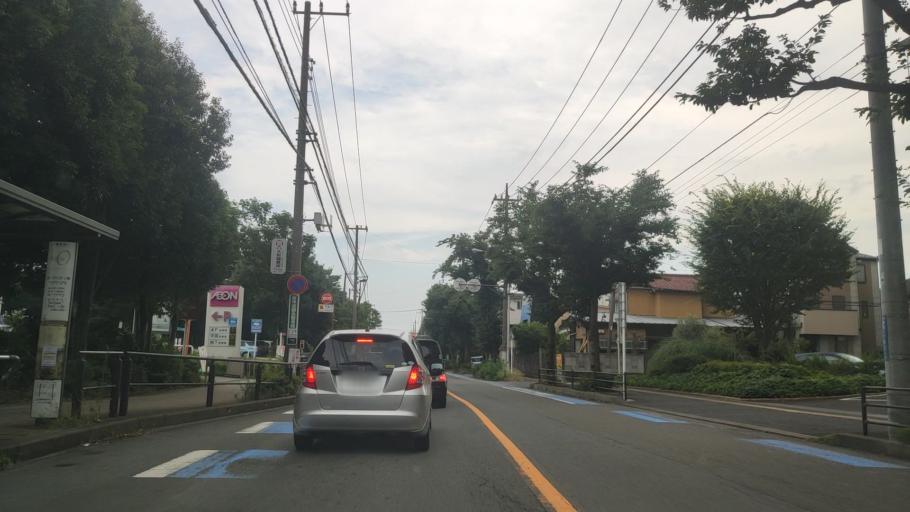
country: JP
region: Kanagawa
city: Minami-rinkan
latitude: 35.4888
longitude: 139.4564
